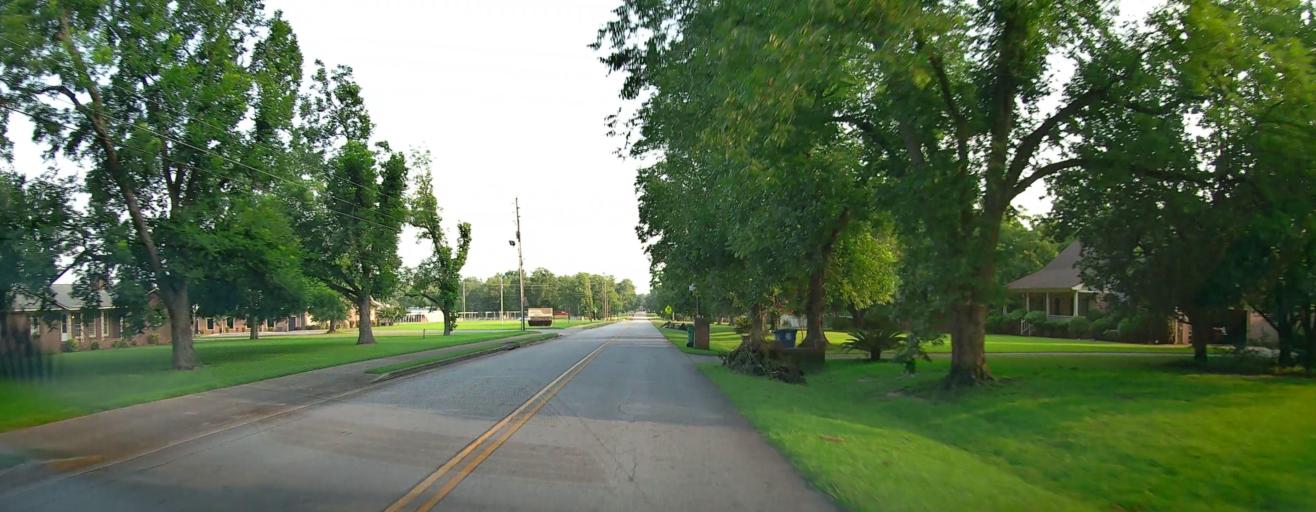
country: US
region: Georgia
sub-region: Peach County
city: Byron
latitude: 32.7399
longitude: -83.6939
